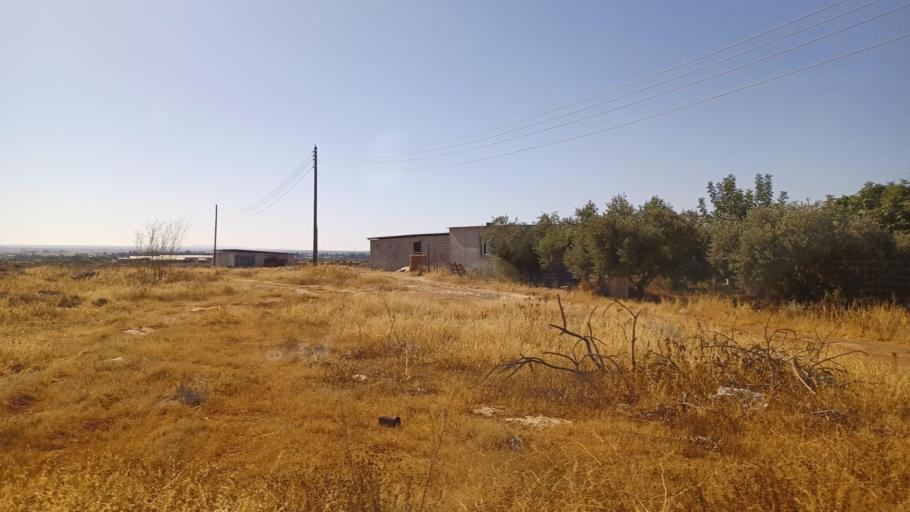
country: CY
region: Larnaka
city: Pergamos
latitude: 35.0516
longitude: 33.6885
